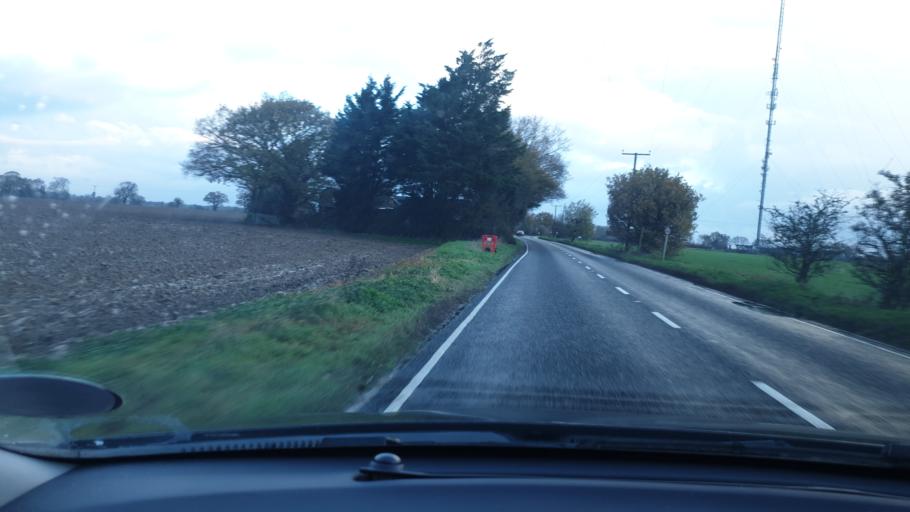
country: GB
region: England
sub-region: Essex
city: Mistley
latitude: 51.9210
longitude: 1.0847
